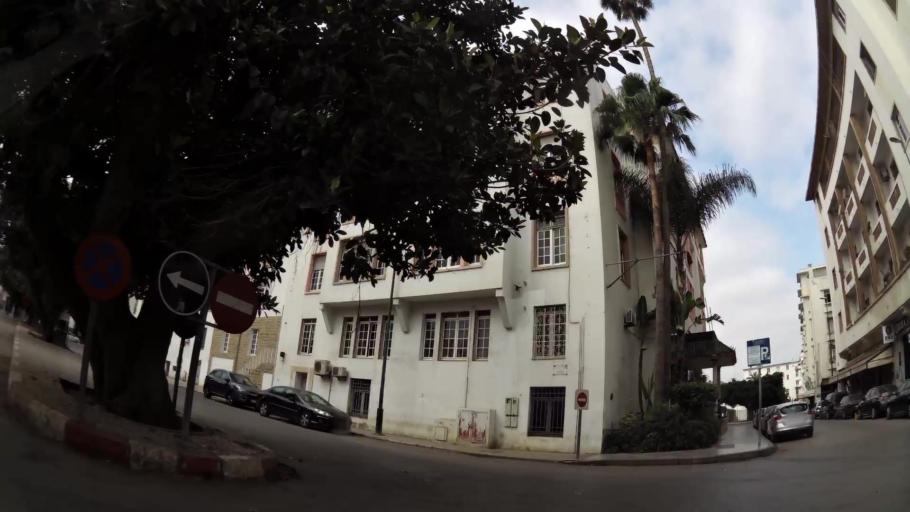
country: MA
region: Rabat-Sale-Zemmour-Zaer
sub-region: Rabat
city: Rabat
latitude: 34.0209
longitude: -6.8353
